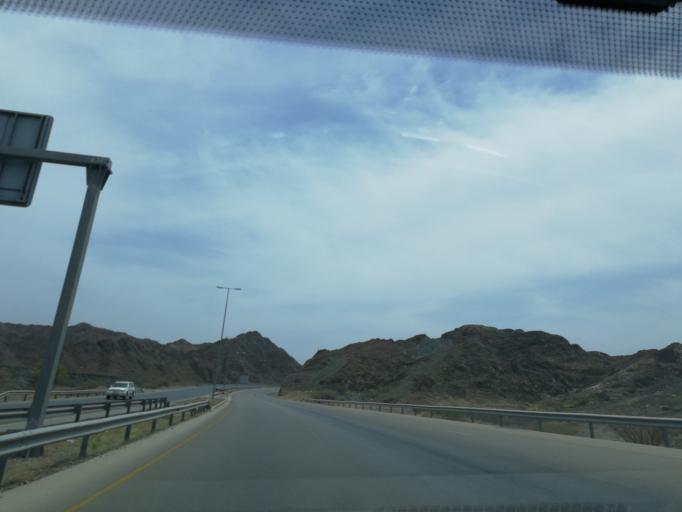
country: OM
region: Muhafazat ad Dakhiliyah
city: Izki
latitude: 22.9704
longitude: 57.7813
